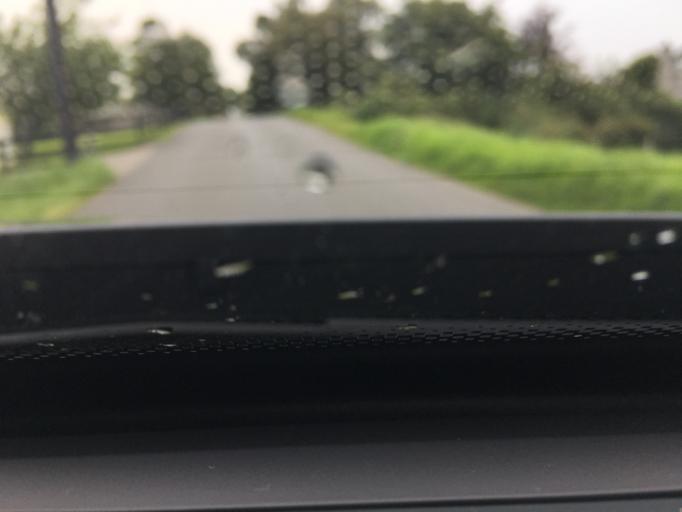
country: GB
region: Northern Ireland
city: Moy
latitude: 54.5144
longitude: -6.6323
